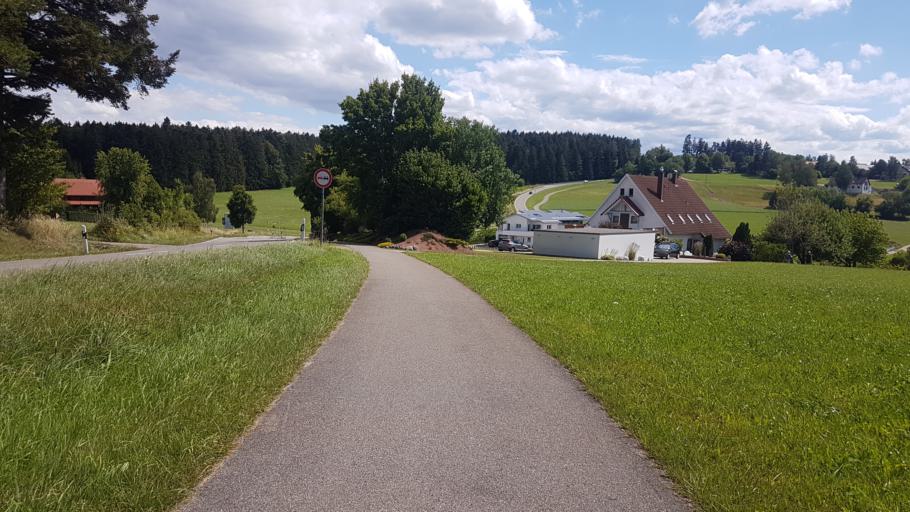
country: DE
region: Baden-Wuerttemberg
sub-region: Freiburg Region
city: Hardt
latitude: 48.1963
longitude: 8.4129
